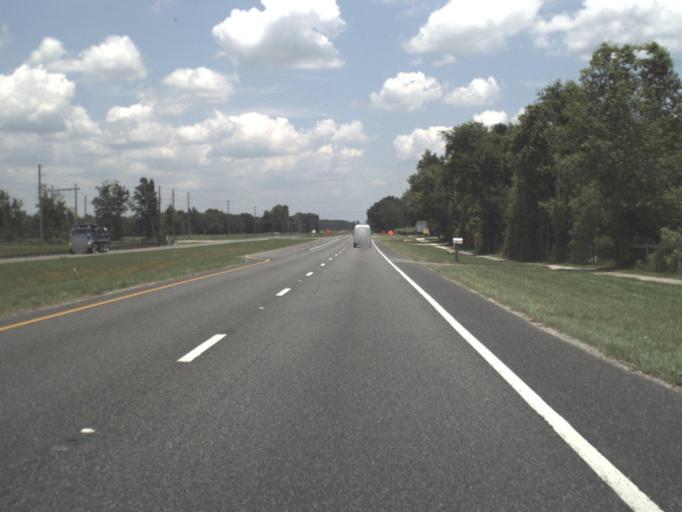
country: US
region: Florida
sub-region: Alachua County
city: Newberry
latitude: 29.6544
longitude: -82.5762
